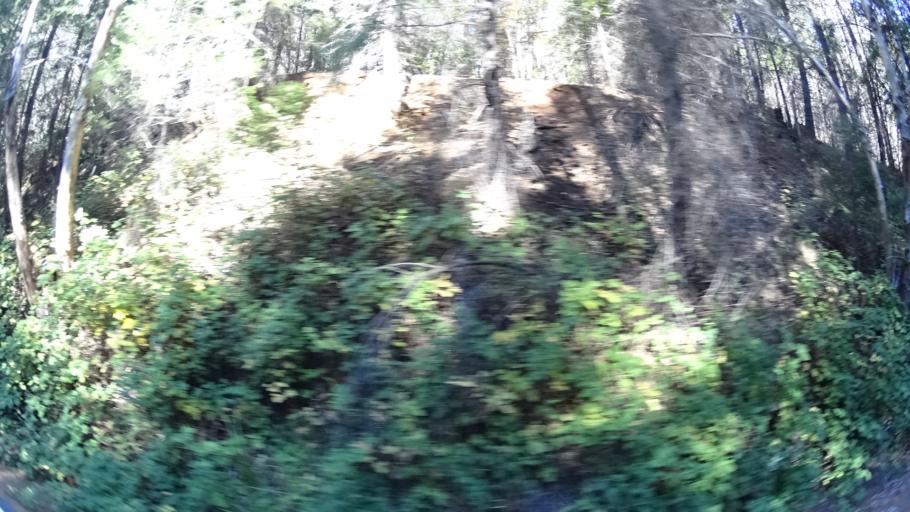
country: US
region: California
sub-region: Trinity County
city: Weaverville
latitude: 41.1920
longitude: -123.0738
